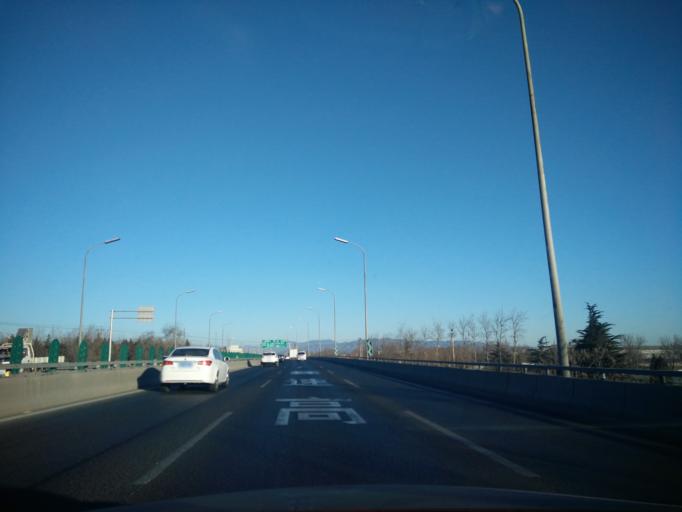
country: CN
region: Beijing
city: Fengtai
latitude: 39.8361
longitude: 116.2272
